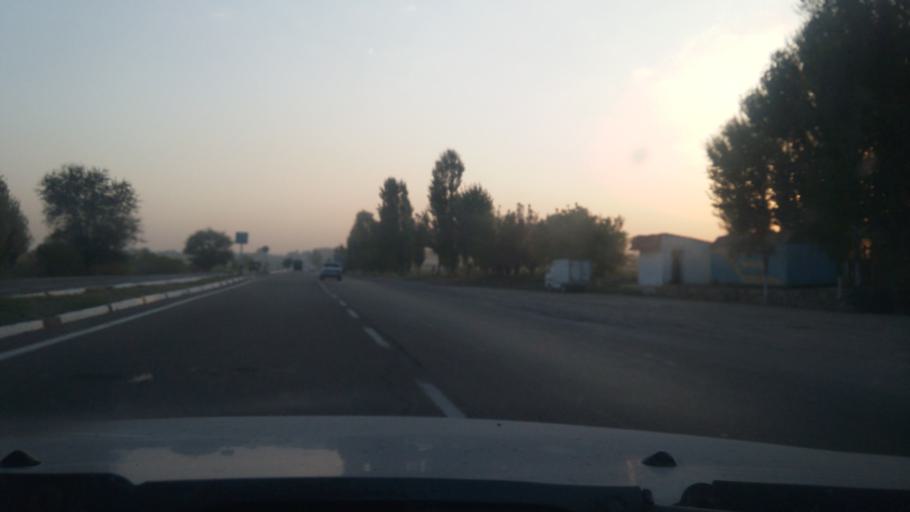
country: UZ
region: Toshkent
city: Yangiyul
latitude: 41.1094
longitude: 68.9794
